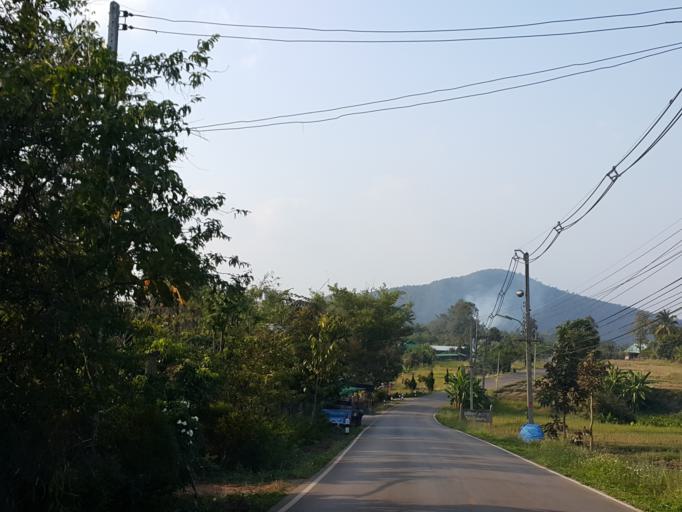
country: TH
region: Chiang Mai
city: Mae On
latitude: 18.8621
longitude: 99.2750
